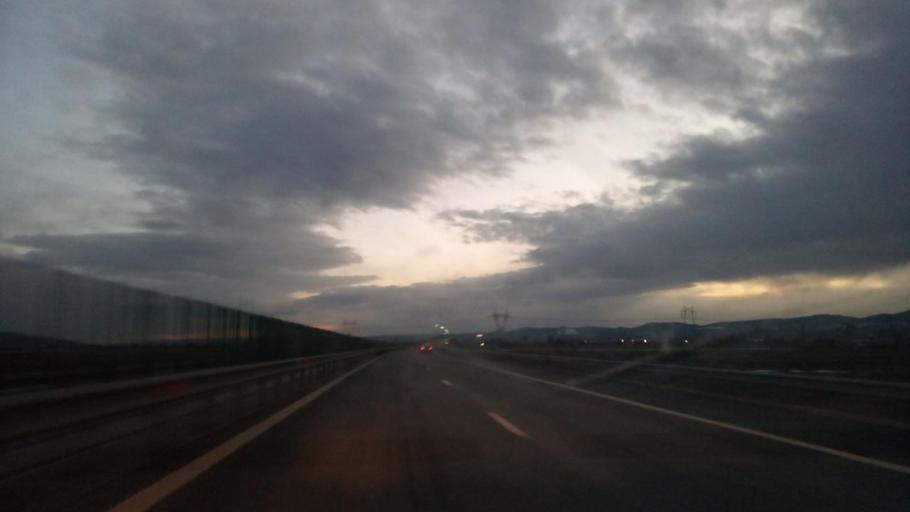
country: RO
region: Bacau
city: Ungureni
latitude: 46.5327
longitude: 26.9691
